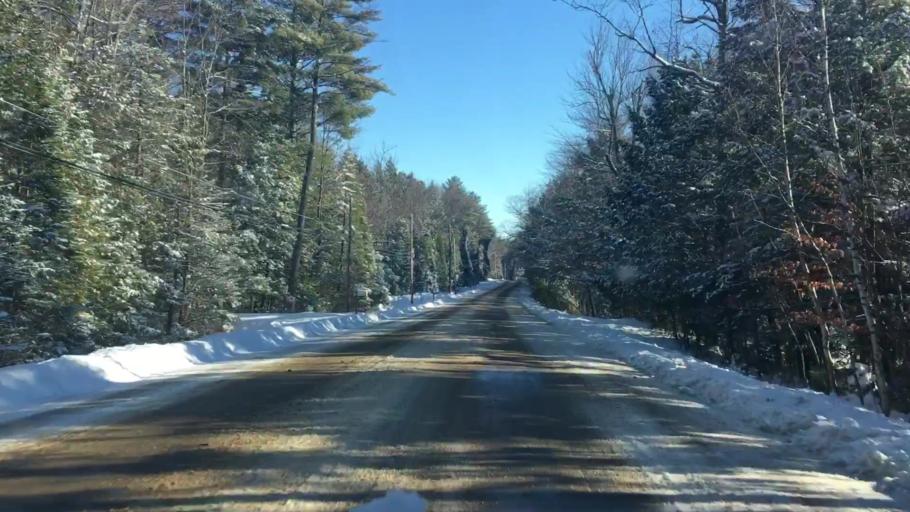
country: US
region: Maine
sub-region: Cumberland County
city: New Gloucester
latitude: 43.9530
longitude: -70.3113
